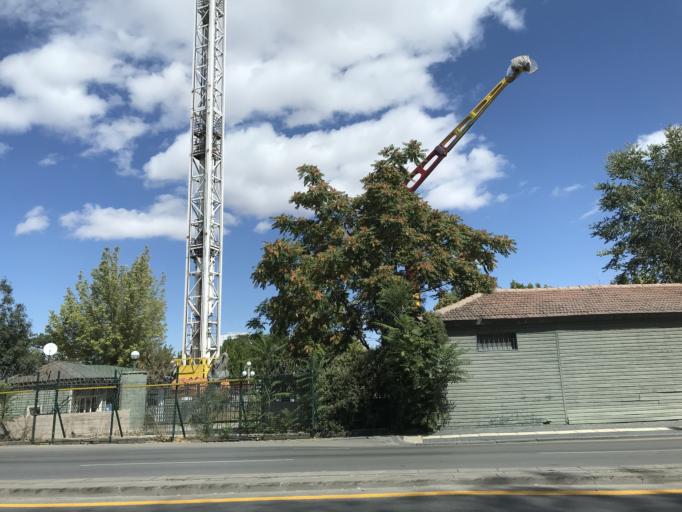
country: TR
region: Ankara
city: Ankara
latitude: 39.9357
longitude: 32.8461
